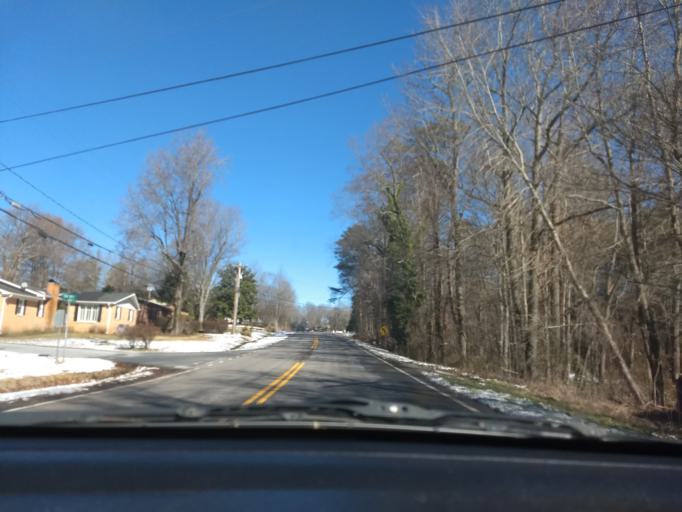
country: US
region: South Carolina
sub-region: Greenville County
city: Wade Hampton
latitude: 34.9081
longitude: -82.3771
